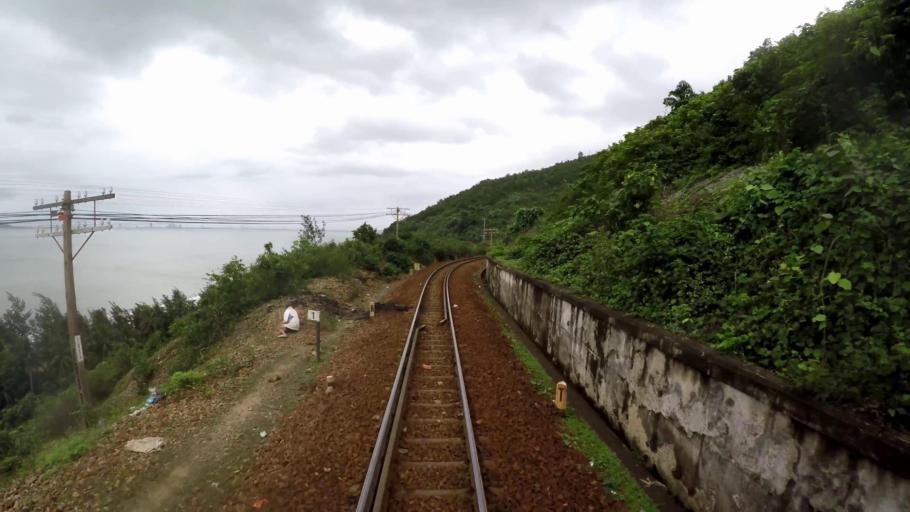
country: VN
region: Da Nang
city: Lien Chieu
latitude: 16.1576
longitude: 108.1351
